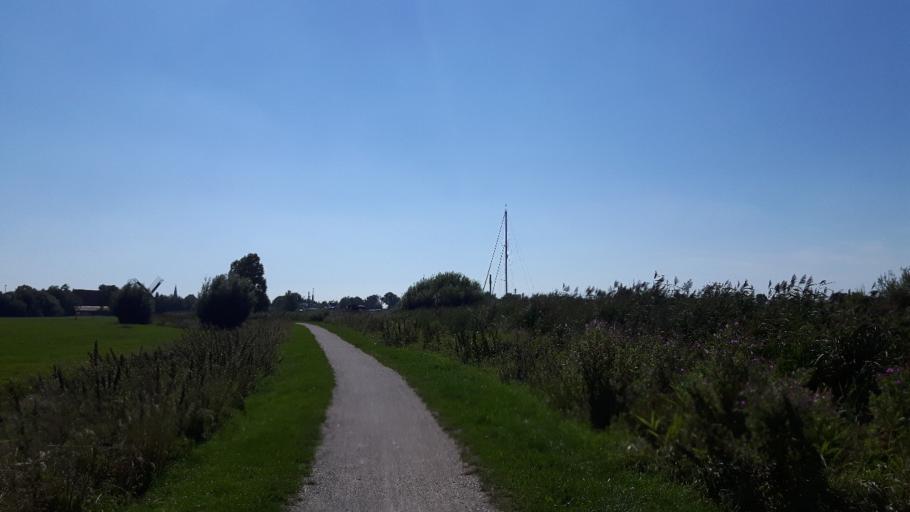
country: NL
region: Friesland
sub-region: Sudwest Fryslan
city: IJlst
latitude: 53.0165
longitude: 5.6305
